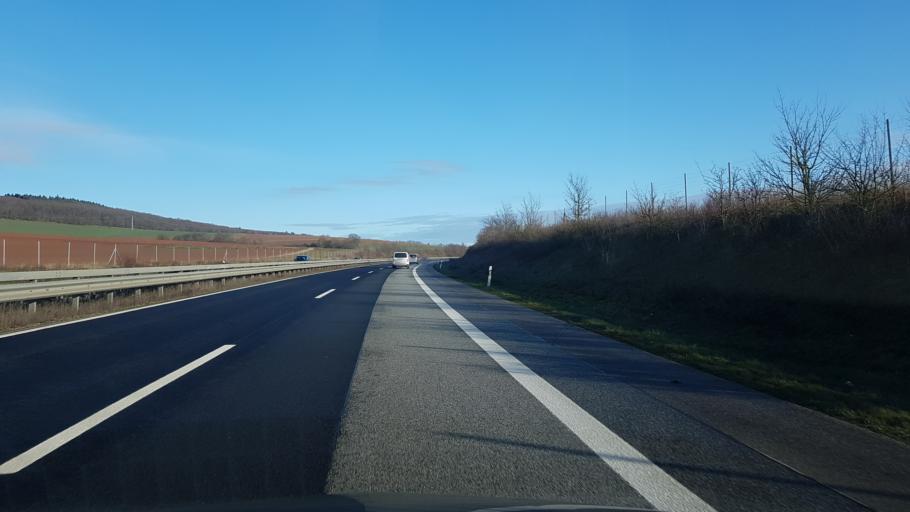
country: DE
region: Rheinland-Pfalz
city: Imsbach
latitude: 49.5748
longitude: 7.9057
